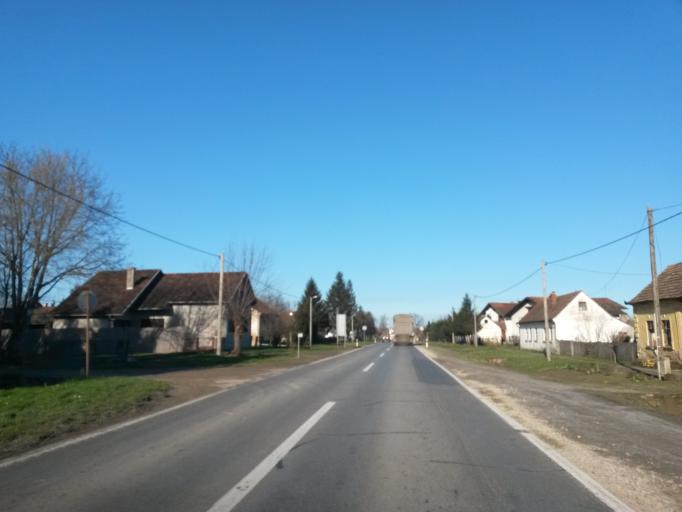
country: HR
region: Virovitick-Podravska
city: Suhopolje
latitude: 45.7625
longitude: 17.5732
